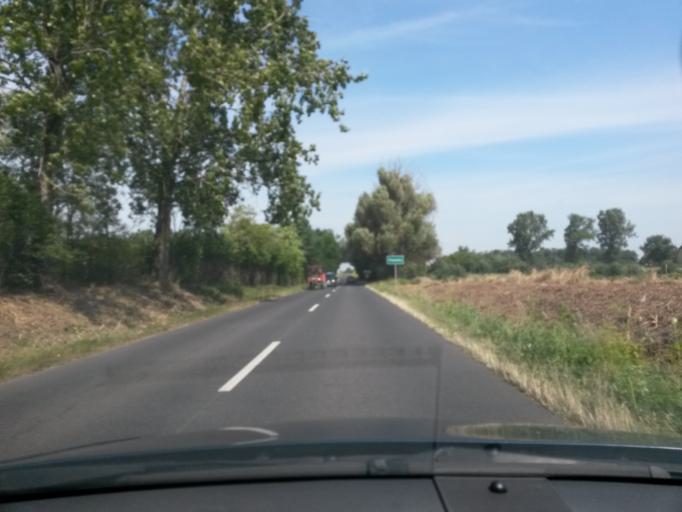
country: PL
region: Lower Silesian Voivodeship
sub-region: Powiat legnicki
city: Legnickie Pole
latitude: 51.1504
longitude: 16.3443
